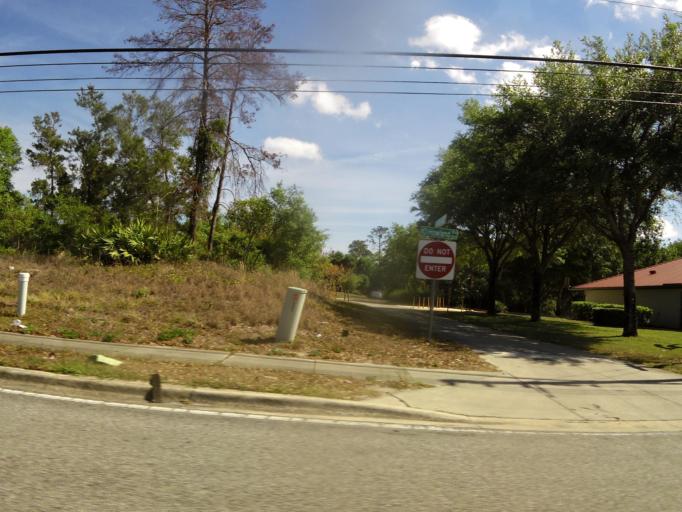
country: US
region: Florida
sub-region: Volusia County
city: Lake Helen
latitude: 28.9425
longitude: -81.2235
